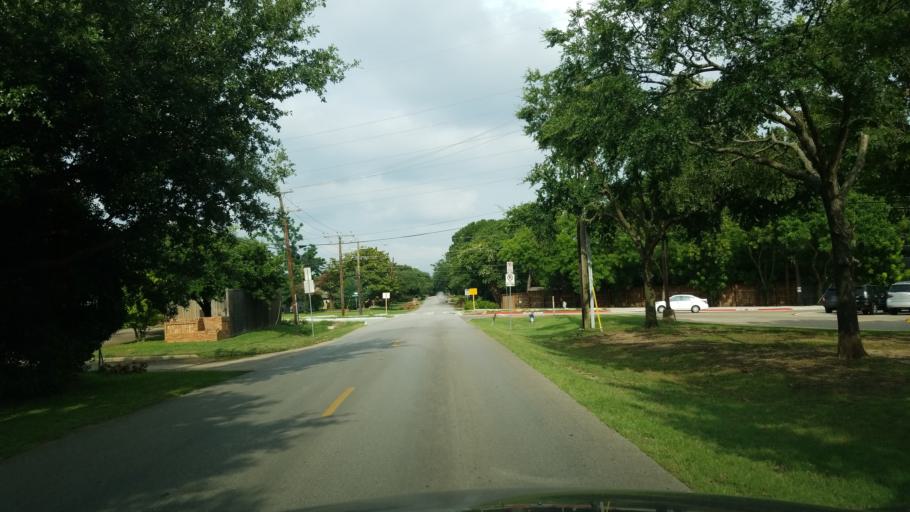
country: US
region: Texas
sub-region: Dallas County
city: Addison
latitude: 32.9022
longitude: -96.8349
